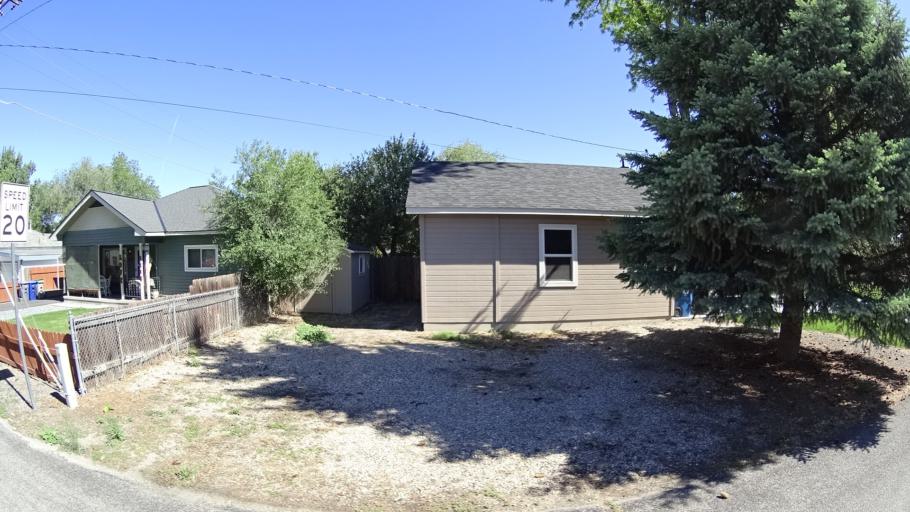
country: US
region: Idaho
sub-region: Ada County
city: Garden City
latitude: 43.6468
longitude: -116.2287
